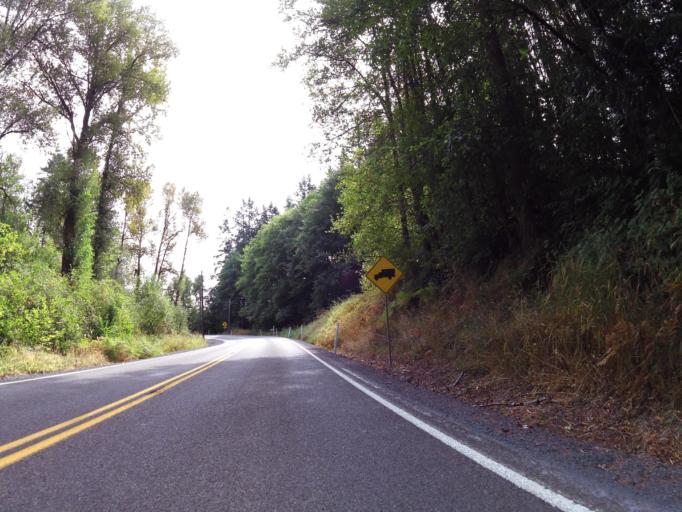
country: US
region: Washington
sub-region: Lewis County
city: Napavine
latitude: 46.5447
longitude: -122.9527
